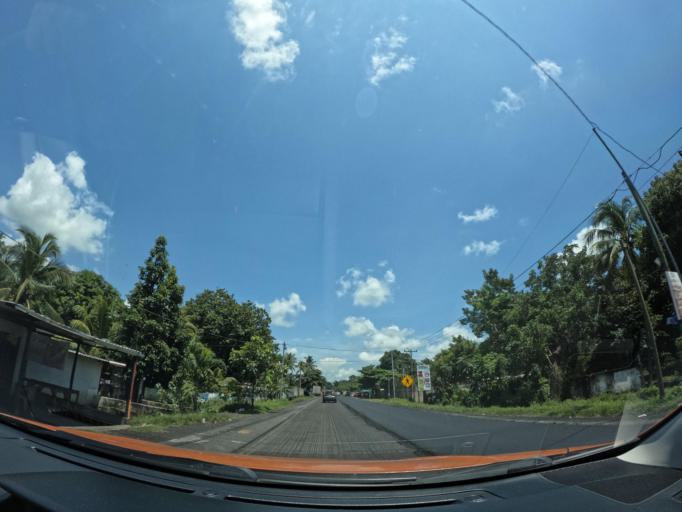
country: GT
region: Escuintla
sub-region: Municipio de Masagua
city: Masagua
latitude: 14.1992
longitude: -90.8516
